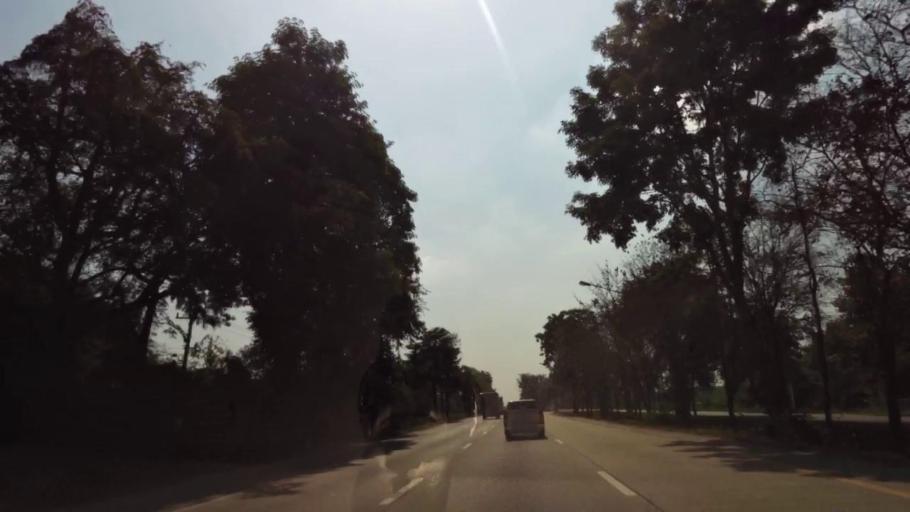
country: TH
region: Phichit
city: Wachira Barami
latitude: 16.5327
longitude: 100.1437
